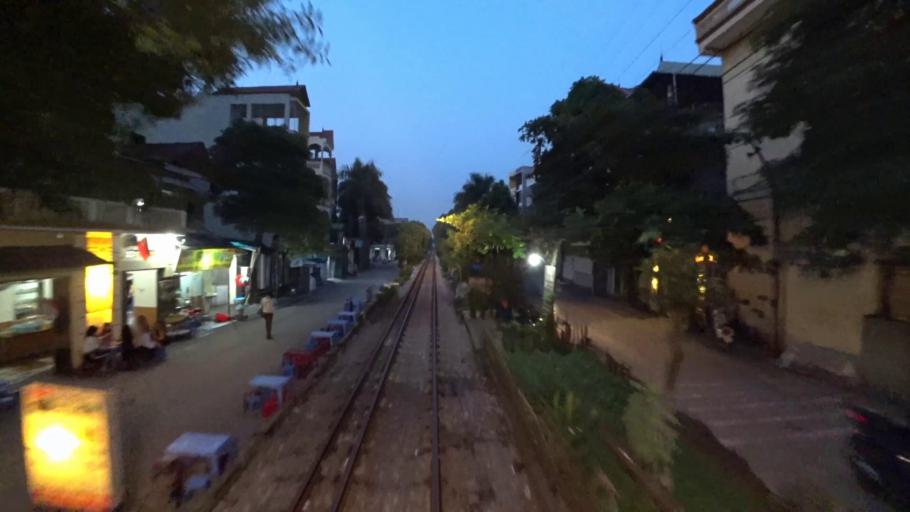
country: VN
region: Ha Noi
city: Soc Son
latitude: 21.2536
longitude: 105.8618
